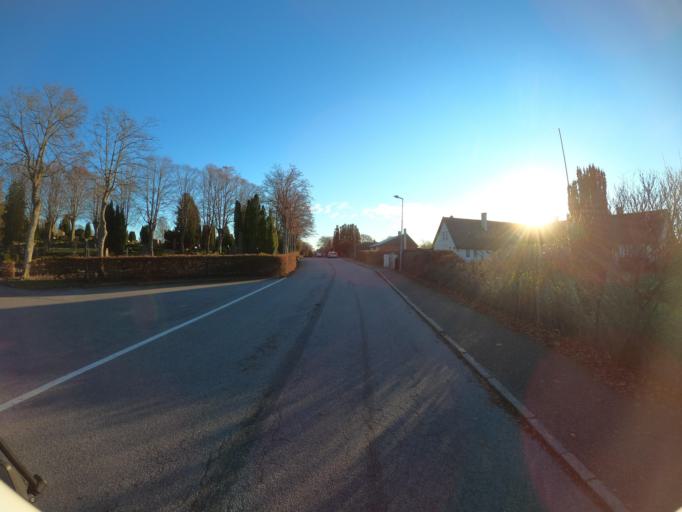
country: SE
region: Skane
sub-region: Svedala Kommun
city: Svedala
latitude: 55.5147
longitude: 13.2176
